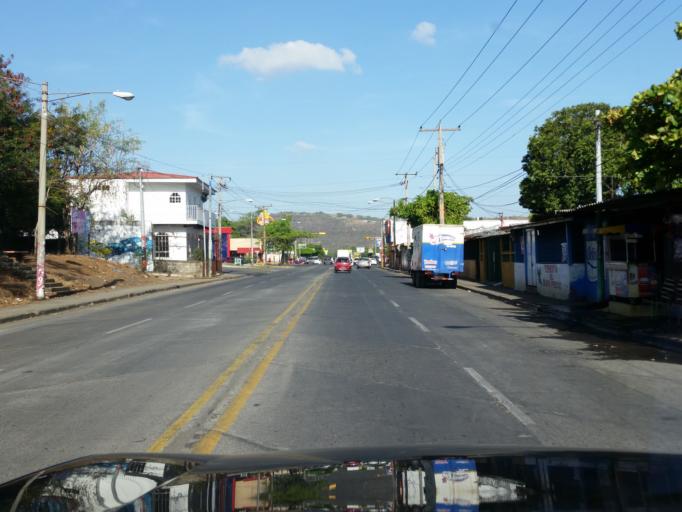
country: NI
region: Managua
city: Ciudad Sandino
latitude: 12.1530
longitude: -86.3033
